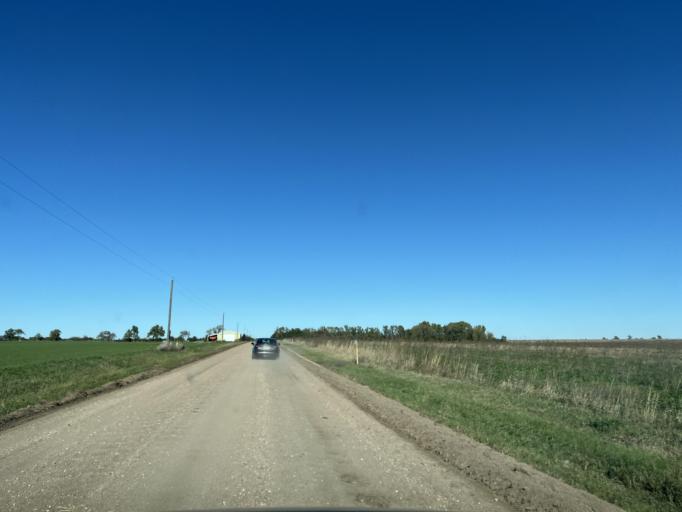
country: US
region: Kansas
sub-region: McPherson County
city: Moundridge
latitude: 38.2070
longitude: -97.6291
